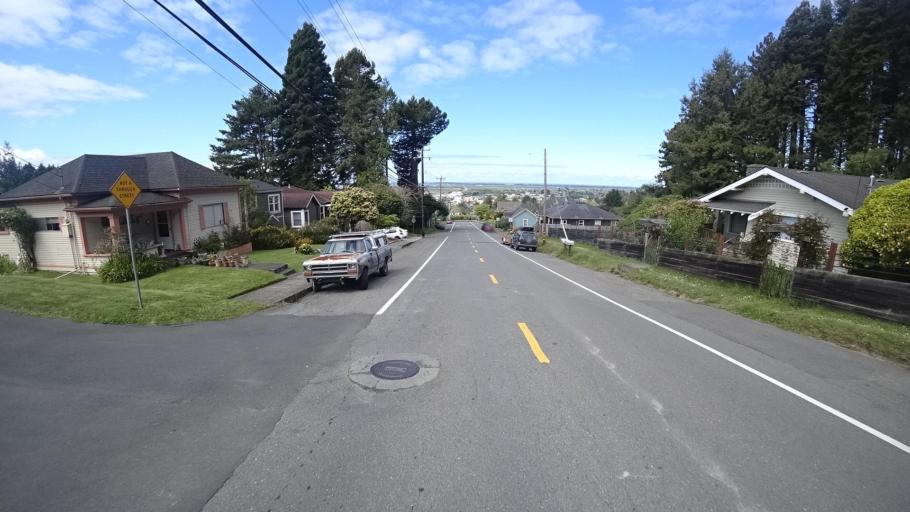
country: US
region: California
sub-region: Humboldt County
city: Arcata
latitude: 40.8678
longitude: -124.0735
